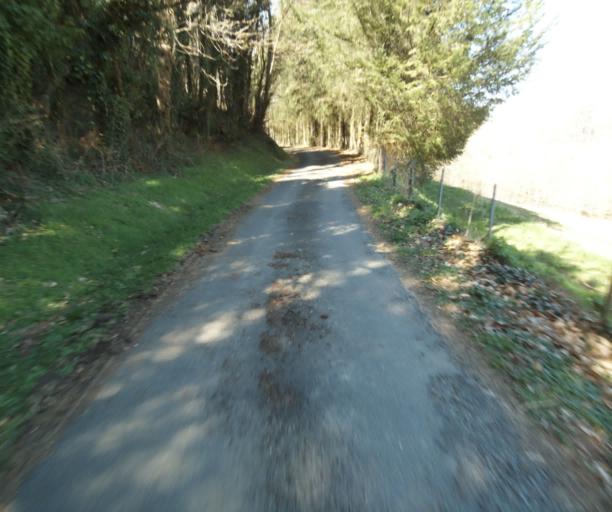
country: FR
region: Limousin
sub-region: Departement de la Correze
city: Chameyrat
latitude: 45.2772
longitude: 1.7042
